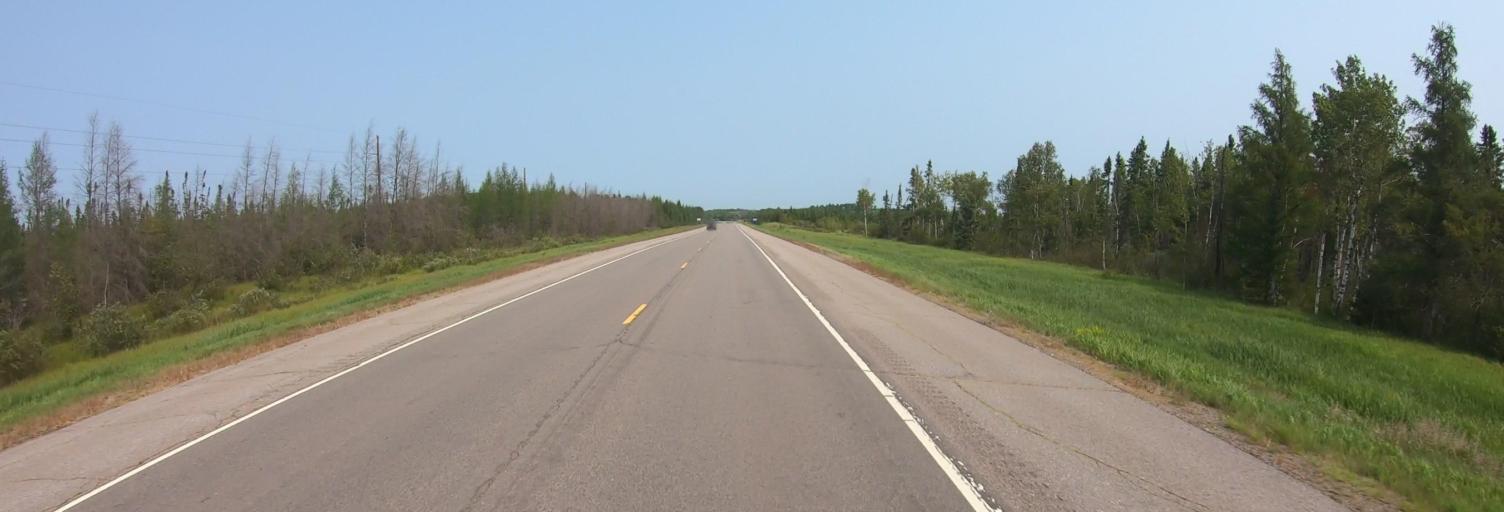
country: US
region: Minnesota
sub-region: Saint Louis County
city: Mountain Iron
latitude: 48.0196
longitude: -92.8306
